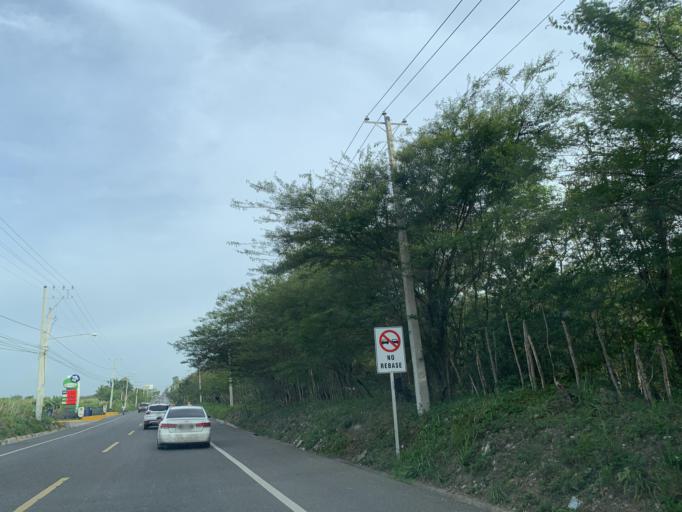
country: DO
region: Puerto Plata
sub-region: Puerto Plata
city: Puerto Plata
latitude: 19.7405
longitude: -70.6332
